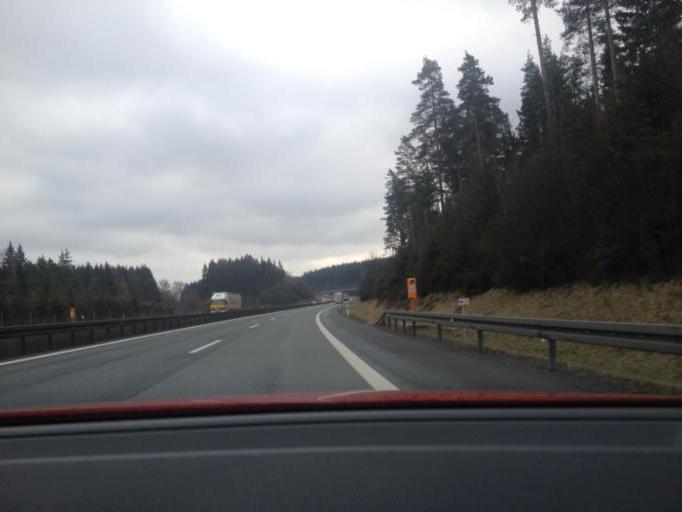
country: DE
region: Bavaria
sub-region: Upper Franconia
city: Schonwald
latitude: 50.2240
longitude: 12.0765
